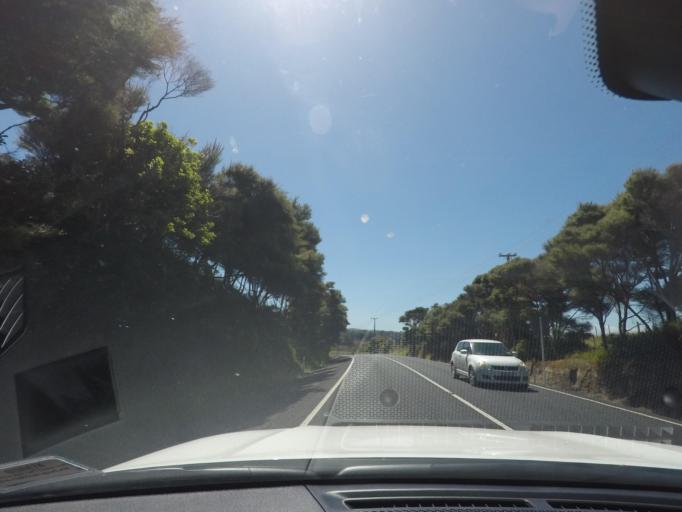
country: NZ
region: Auckland
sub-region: Auckland
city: Parakai
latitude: -36.6259
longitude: 174.3603
